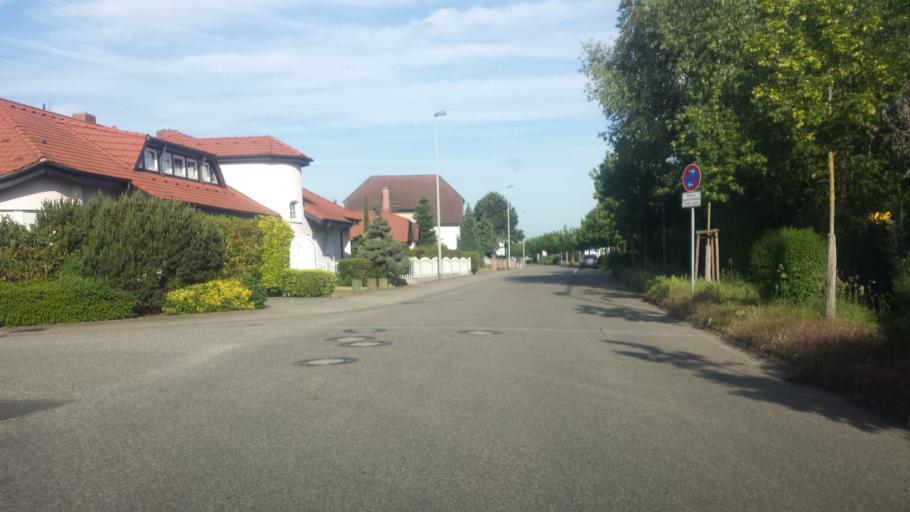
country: DE
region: Hesse
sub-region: Regierungsbezirk Darmstadt
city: Burstadt
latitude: 49.6497
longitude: 8.4664
